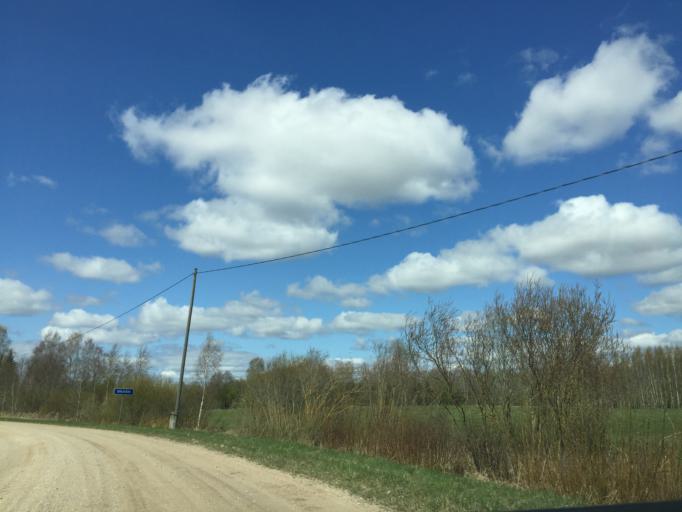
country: LV
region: Vilanu
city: Vilani
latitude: 56.6519
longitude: 27.1318
